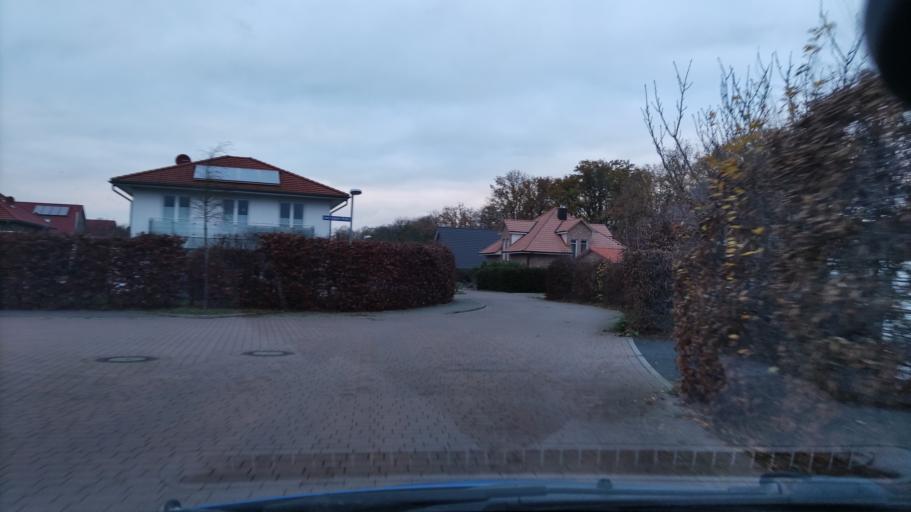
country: DE
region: Lower Saxony
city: Reppenstedt
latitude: 53.2554
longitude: 10.3774
